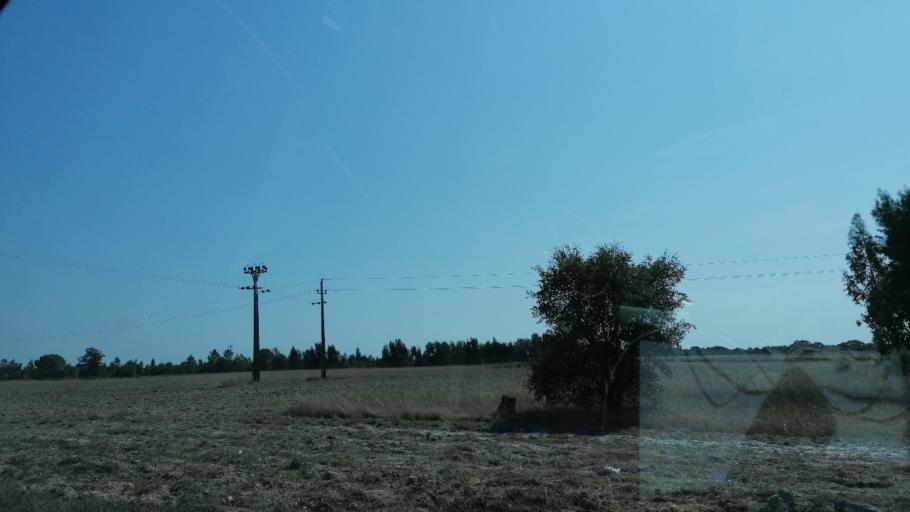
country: PT
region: Santarem
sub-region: Benavente
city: Poceirao
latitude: 38.7261
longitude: -8.6435
